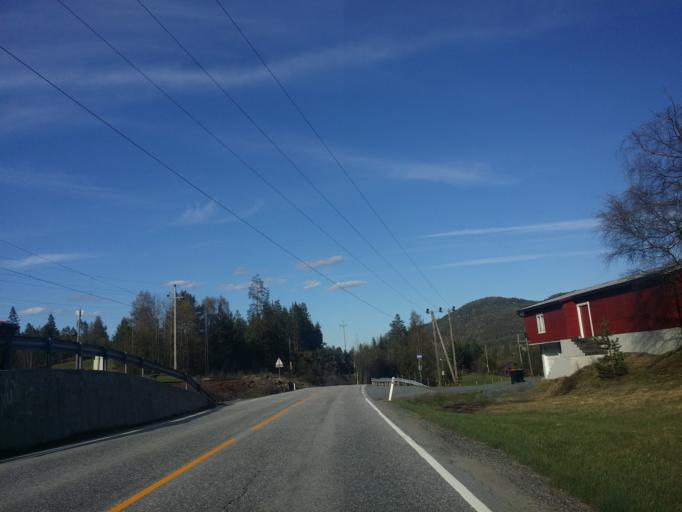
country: NO
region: Telemark
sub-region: Notodden
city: Notodden
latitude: 59.6105
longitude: 9.4516
